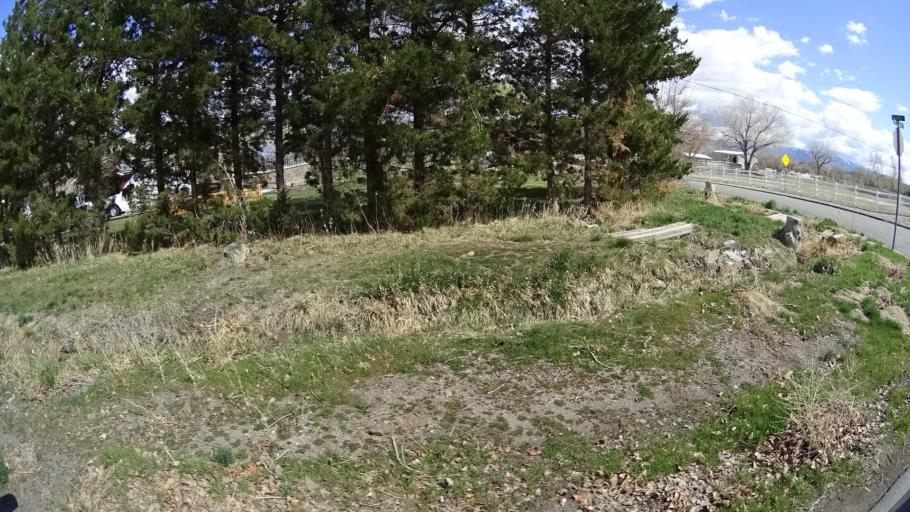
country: US
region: Nevada
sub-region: Washoe County
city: Reno
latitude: 39.4341
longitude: -119.7893
